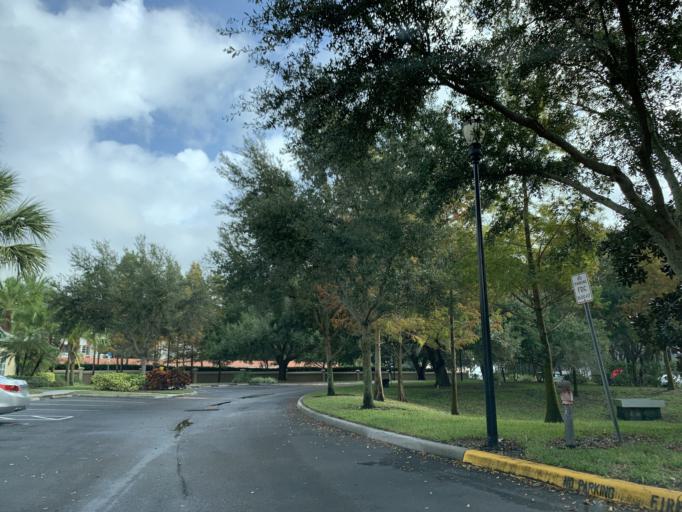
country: US
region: Florida
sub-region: Pinellas County
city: South Highpoint
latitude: 27.9533
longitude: -82.7258
